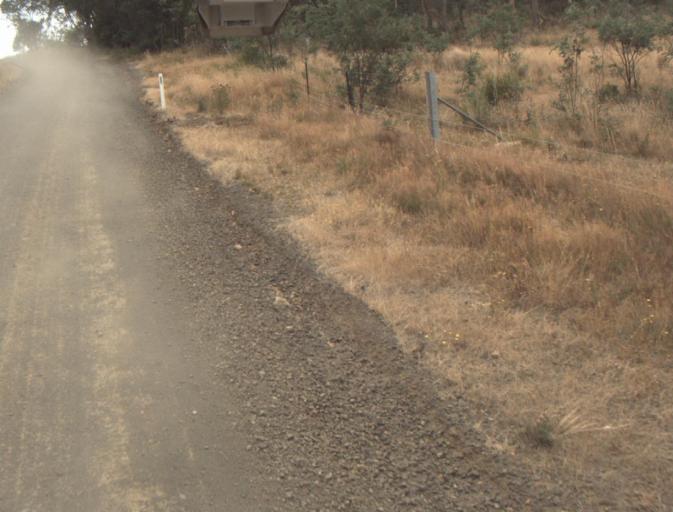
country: AU
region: Tasmania
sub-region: Northern Midlands
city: Evandale
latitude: -41.5206
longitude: 147.3731
